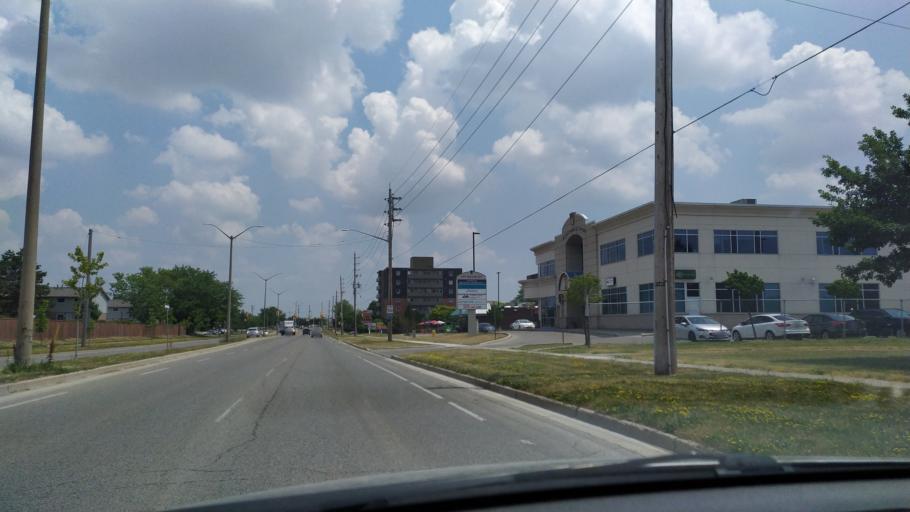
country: CA
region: Ontario
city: London
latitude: 42.9342
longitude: -81.2308
